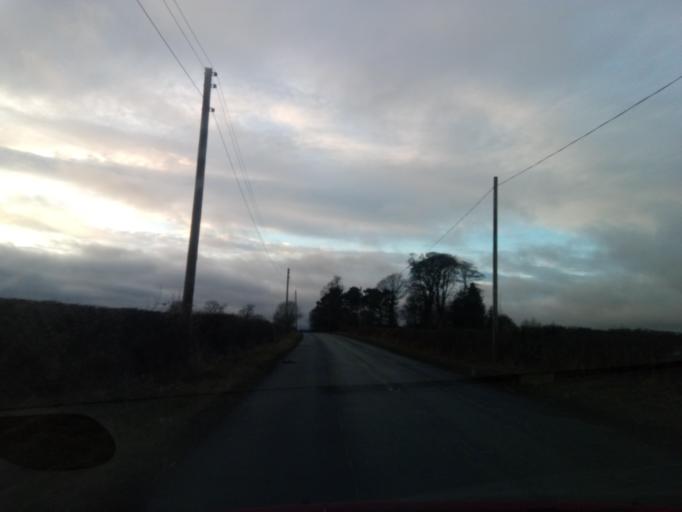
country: GB
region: England
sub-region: Northumberland
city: Meldon
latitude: 55.1330
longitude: -1.7794
